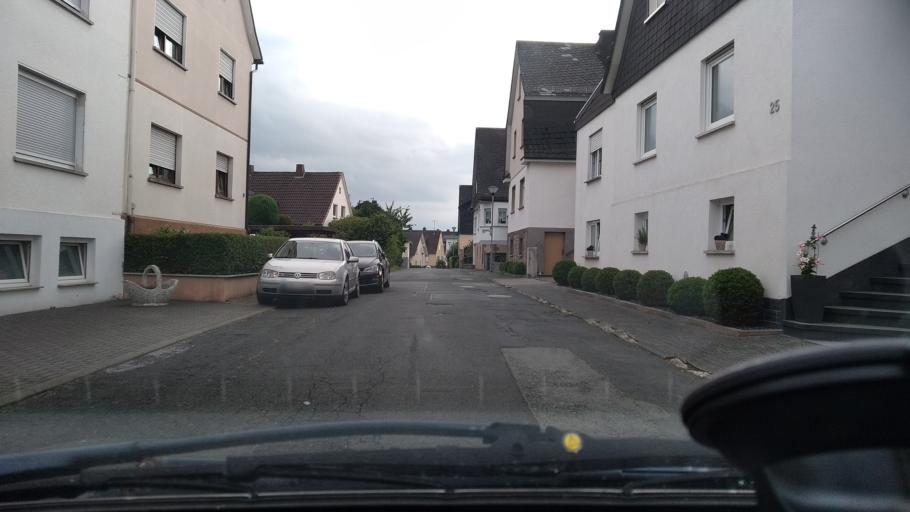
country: DE
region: Hesse
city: Dillenburg
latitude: 50.7768
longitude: 8.3039
